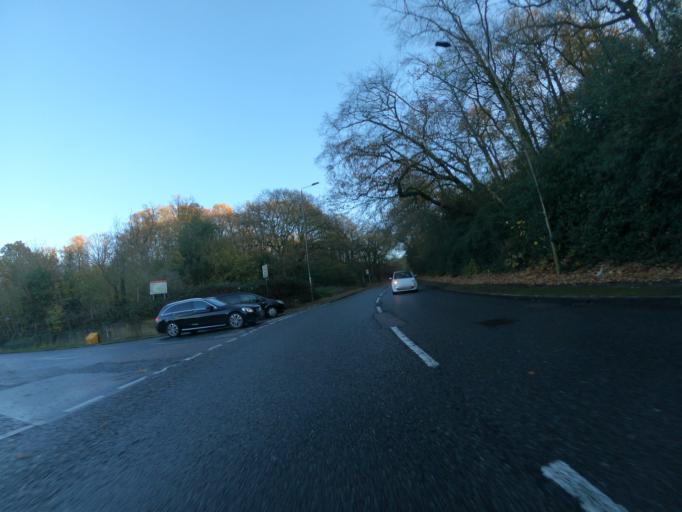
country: GB
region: England
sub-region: Greater London
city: Abbey Wood
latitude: 51.4836
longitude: 0.1101
